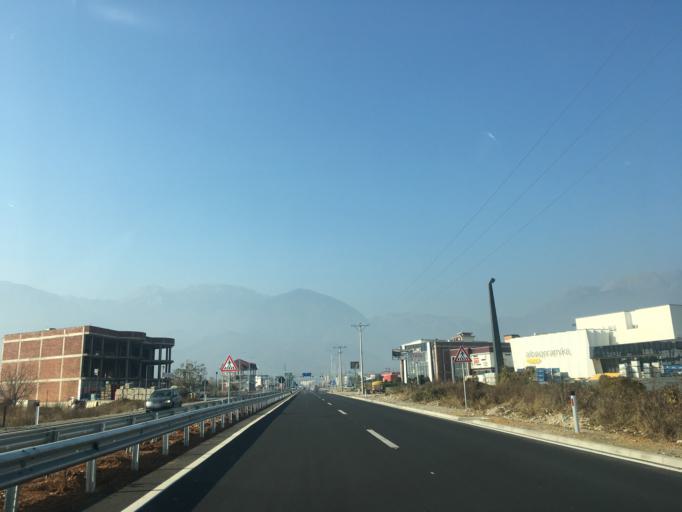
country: XK
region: Pec
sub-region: Komuna e Pejes
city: Peje
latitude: 42.6572
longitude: 20.3310
